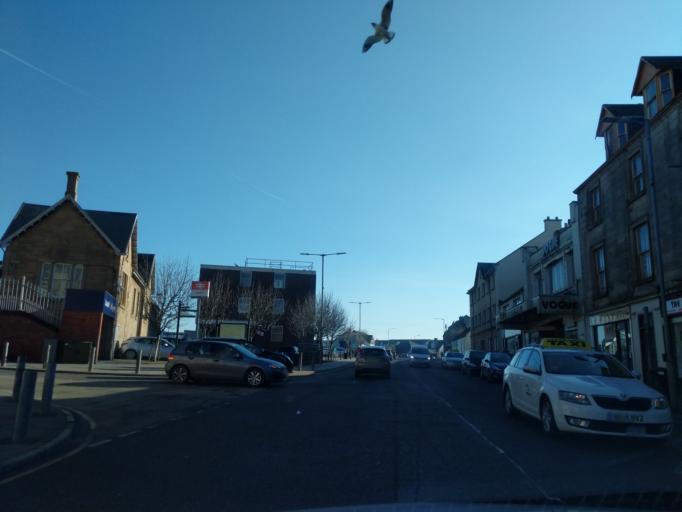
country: GB
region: Scotland
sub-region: South Lanarkshire
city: Lanark
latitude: 55.6735
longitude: -3.7742
